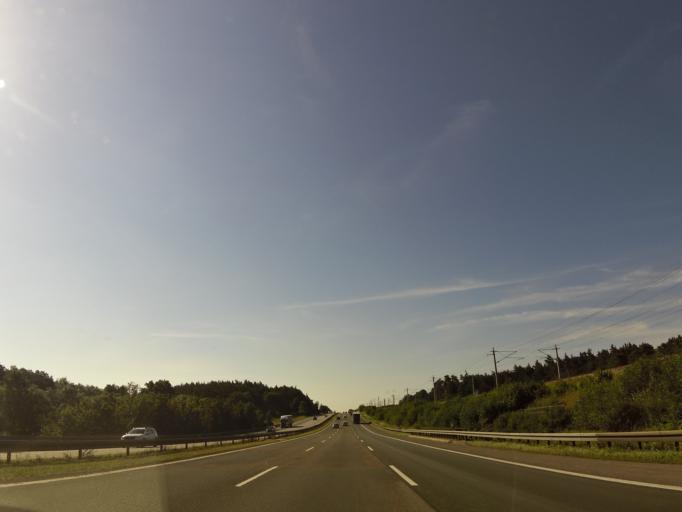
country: DE
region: Bavaria
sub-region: Regierungsbezirk Mittelfranken
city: Allersberg
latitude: 49.2072
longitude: 11.2344
